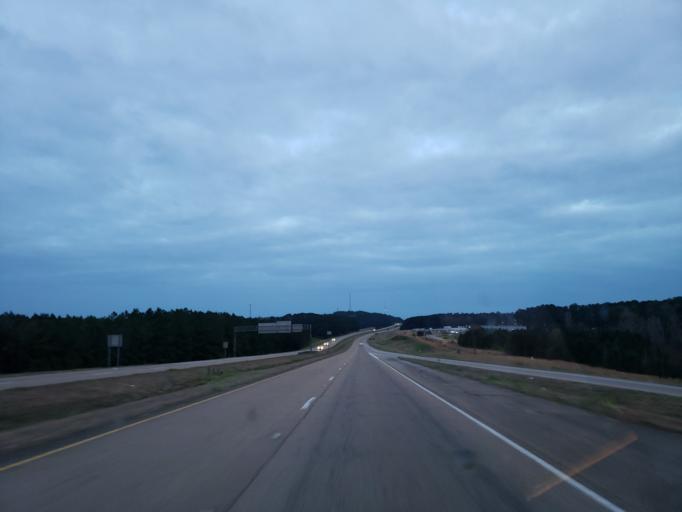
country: US
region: Mississippi
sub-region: Lauderdale County
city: Marion
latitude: 32.3803
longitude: -88.6363
